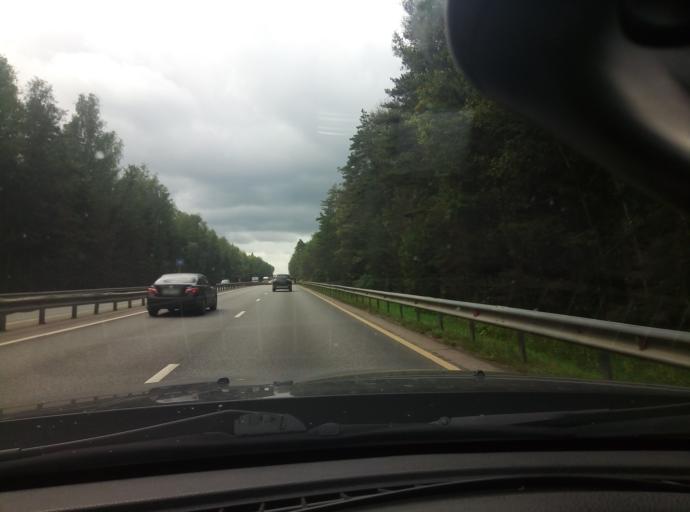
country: RU
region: Kaluga
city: Maloyaroslavets
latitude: 55.0196
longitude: 36.5594
